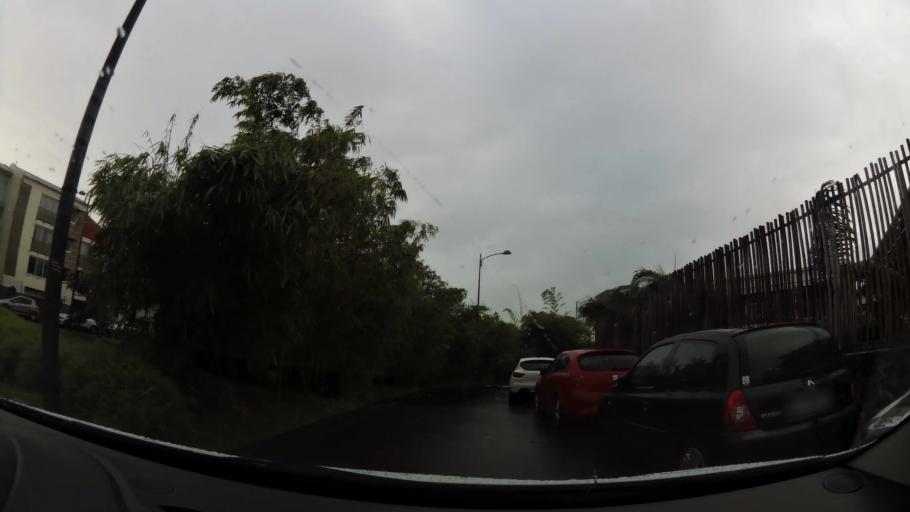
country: RE
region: Reunion
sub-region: Reunion
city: Saint-Andre
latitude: -20.9758
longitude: 55.6504
